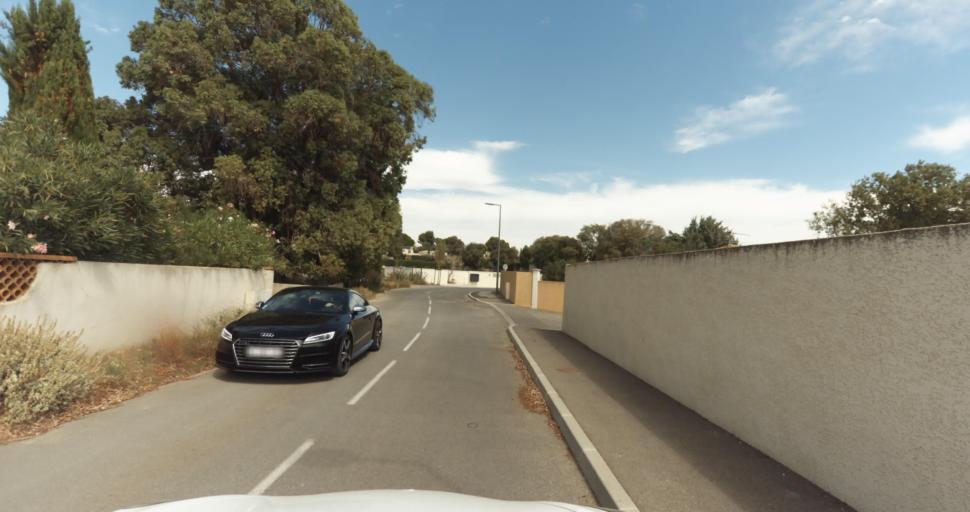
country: FR
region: Provence-Alpes-Cote d'Azur
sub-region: Departement des Bouches-du-Rhone
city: Miramas
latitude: 43.5788
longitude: 5.0199
